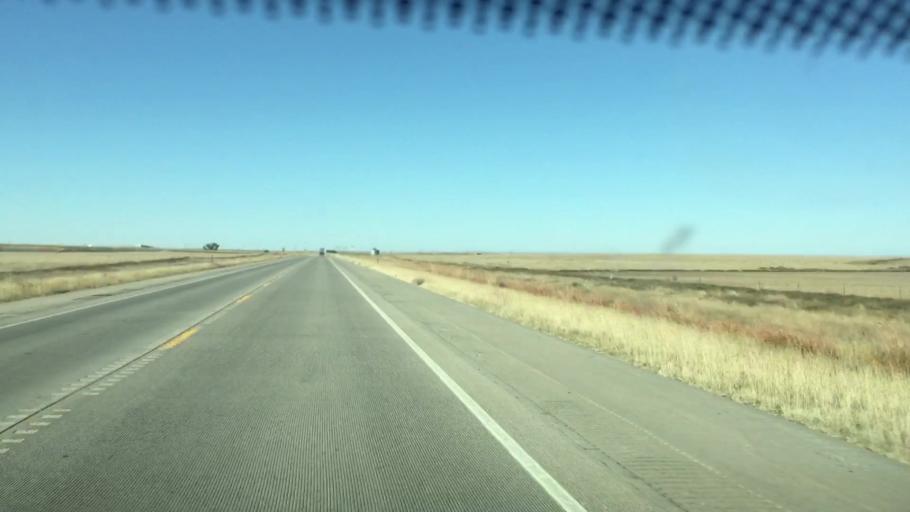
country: US
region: Colorado
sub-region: Kiowa County
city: Eads
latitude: 38.7531
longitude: -102.7768
